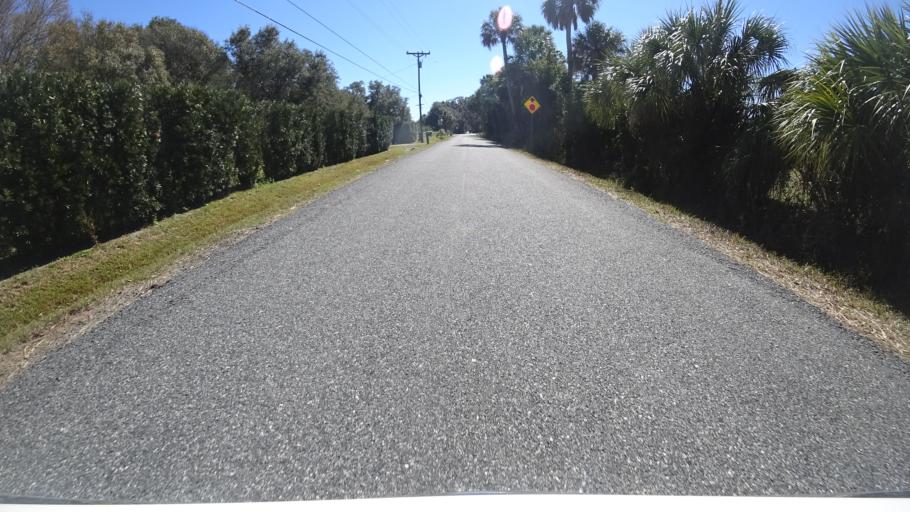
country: US
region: Florida
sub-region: Manatee County
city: Memphis
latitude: 27.5482
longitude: -82.5401
